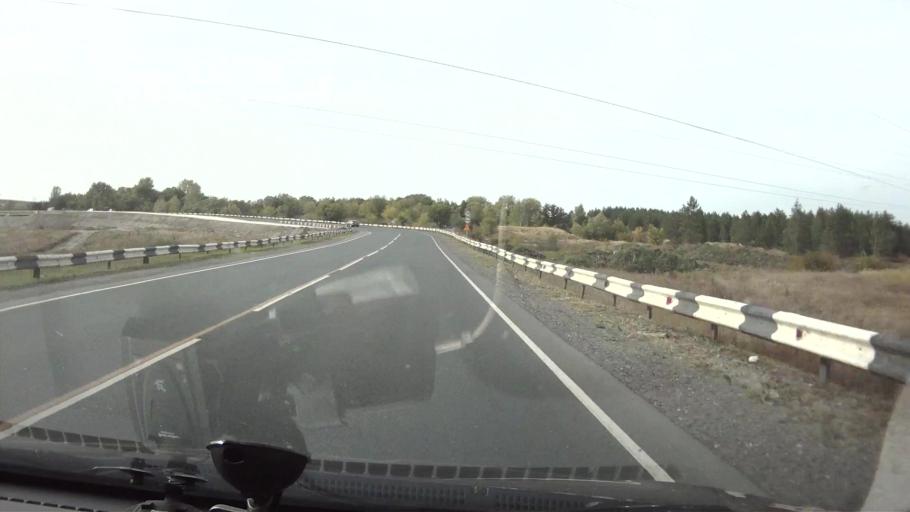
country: RU
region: Saratov
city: Sennoy
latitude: 52.1430
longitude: 46.9078
